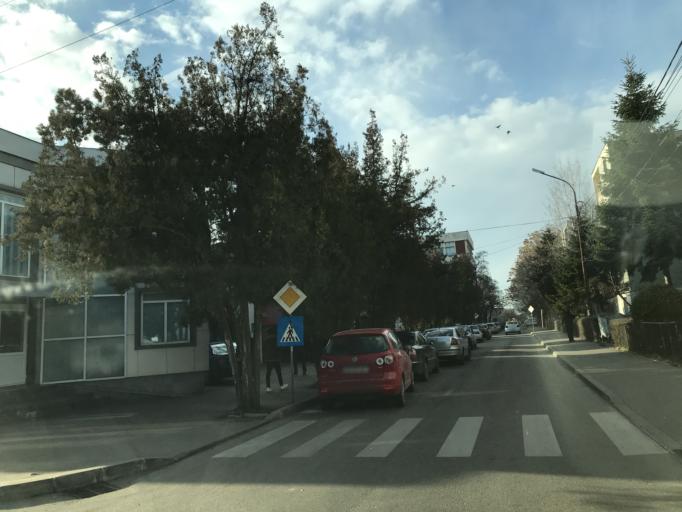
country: RO
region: Olt
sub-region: Municipiul Slatina
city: Slatina
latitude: 44.4267
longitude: 24.3656
